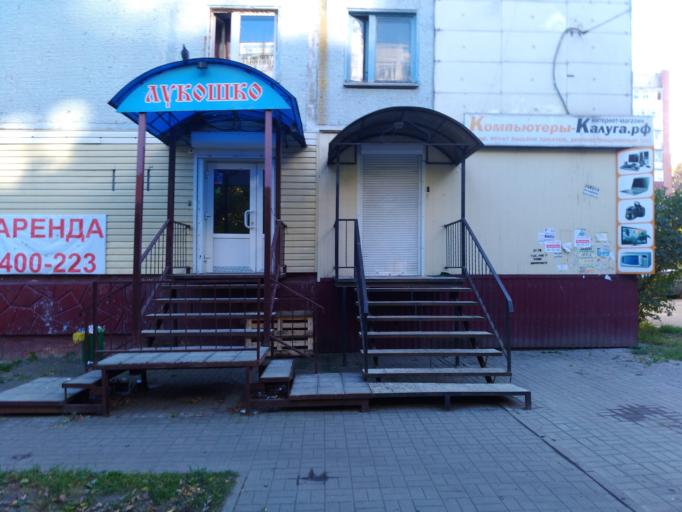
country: RU
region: Kaluga
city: Kaluga
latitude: 54.5182
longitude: 36.2688
